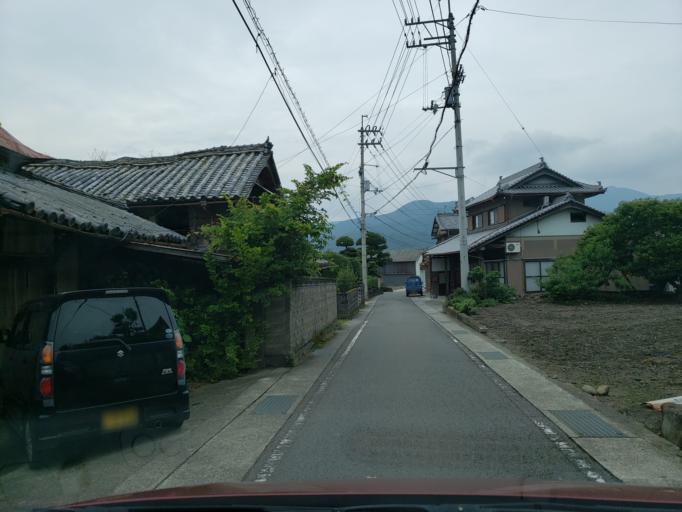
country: JP
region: Tokushima
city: Kamojimacho-jogejima
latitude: 34.1001
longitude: 134.2805
